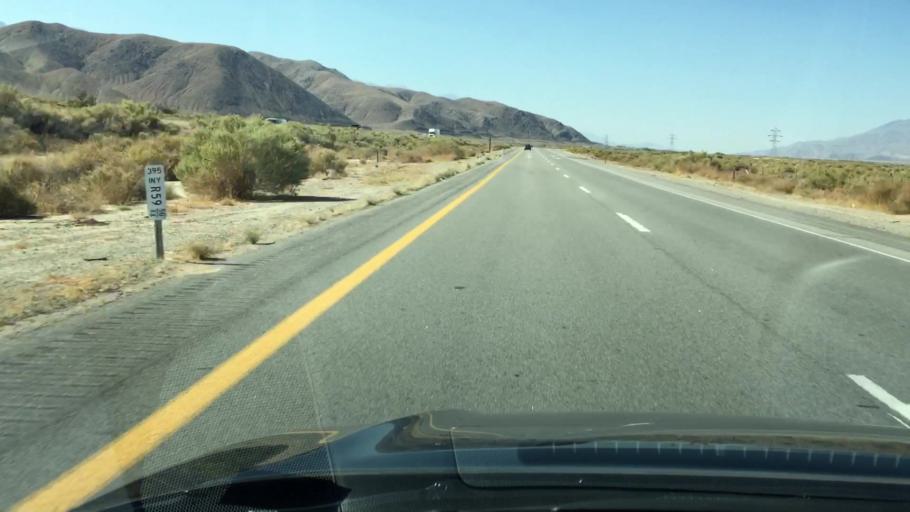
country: US
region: California
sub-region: Inyo County
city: Lone Pine
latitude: 36.6291
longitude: -118.0740
